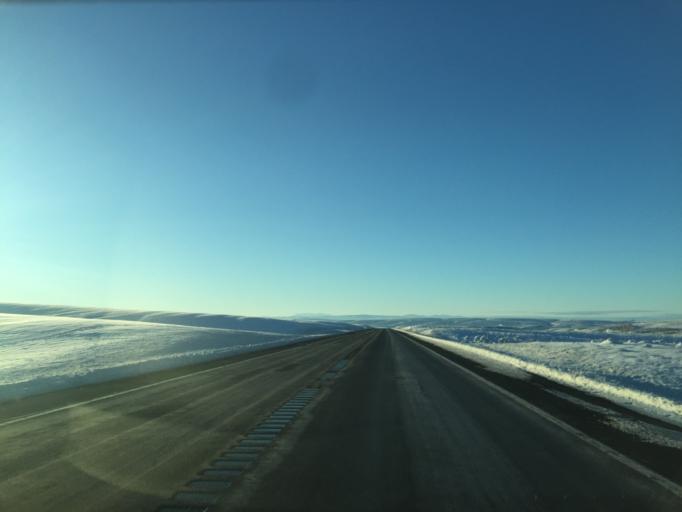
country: US
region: Washington
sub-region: Grant County
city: Soap Lake
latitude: 47.5994
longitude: -119.5984
